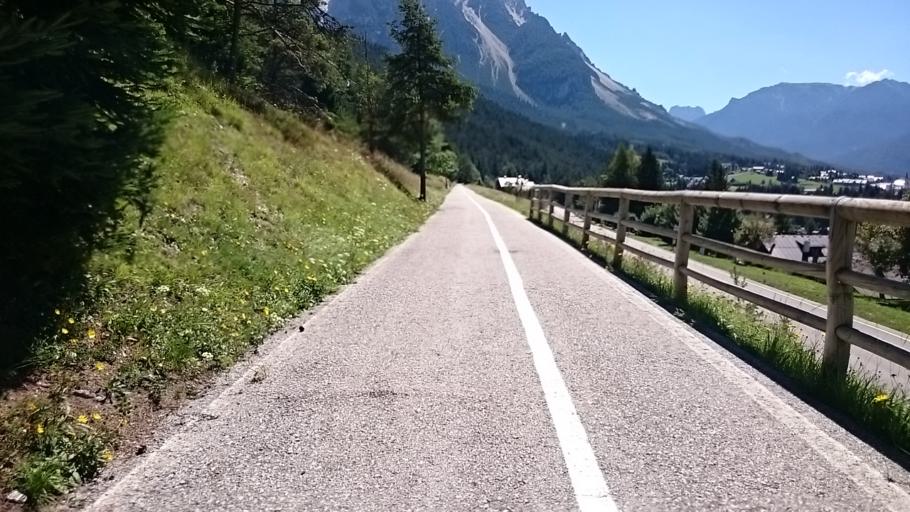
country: IT
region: Veneto
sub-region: Provincia di Belluno
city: San Vito
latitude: 46.4775
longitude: 12.1986
